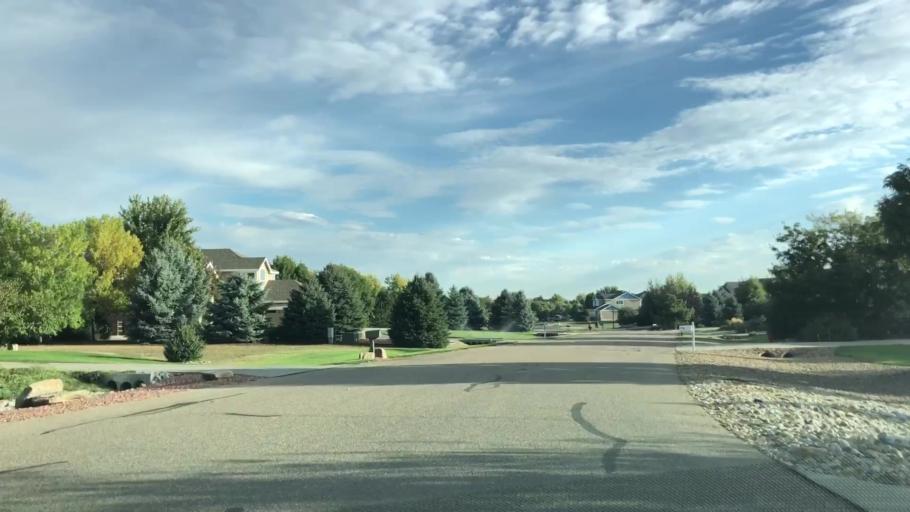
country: US
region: Colorado
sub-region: Weld County
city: Windsor
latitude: 40.4403
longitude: -104.9620
